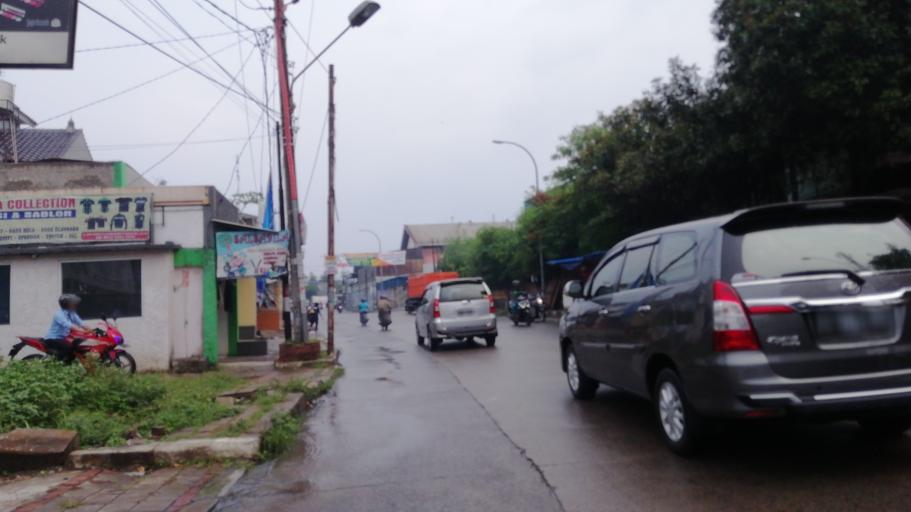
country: ID
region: West Java
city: Bogor
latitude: -6.5458
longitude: 106.8059
